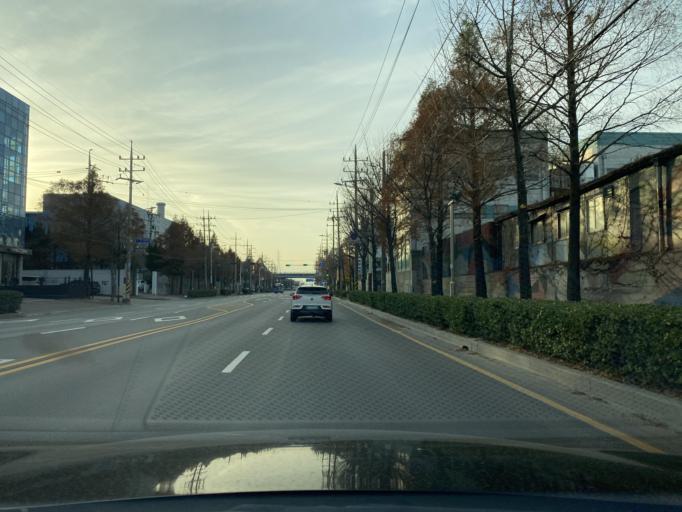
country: KR
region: Incheon
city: Incheon
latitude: 37.4993
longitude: 126.6522
